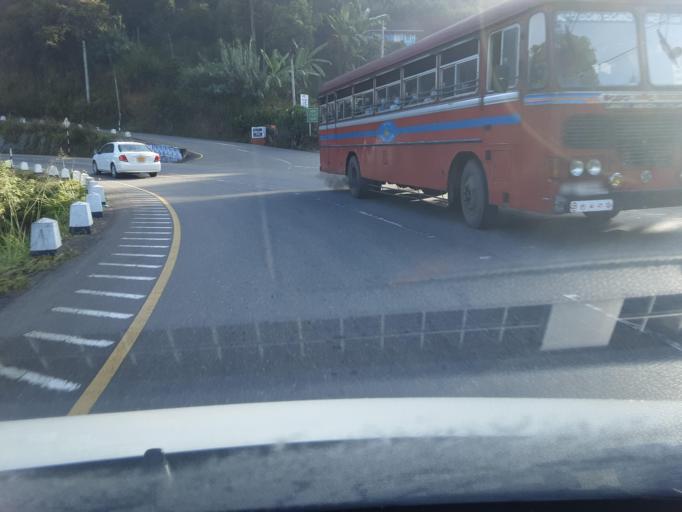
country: LK
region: Uva
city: Haputale
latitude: 6.9106
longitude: 80.9314
